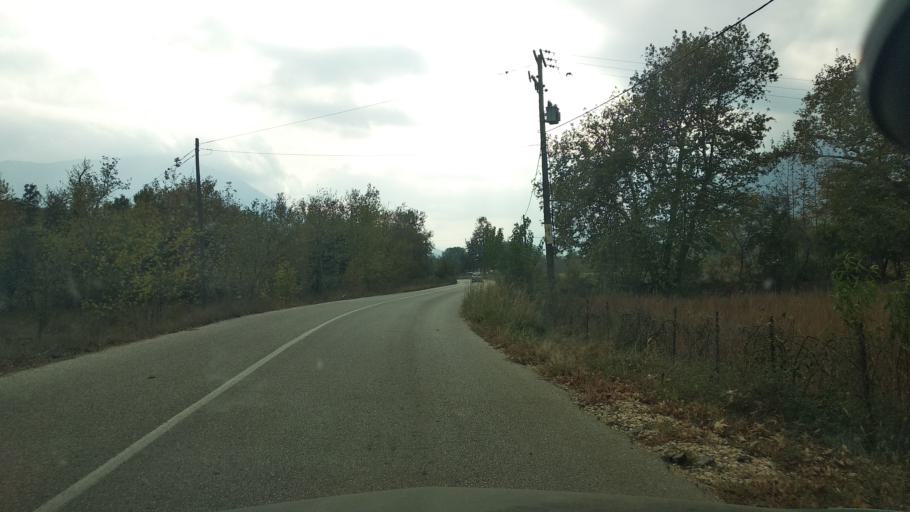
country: GR
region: Thessaly
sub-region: Trikala
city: Kastraki
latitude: 39.7207
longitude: 21.5265
